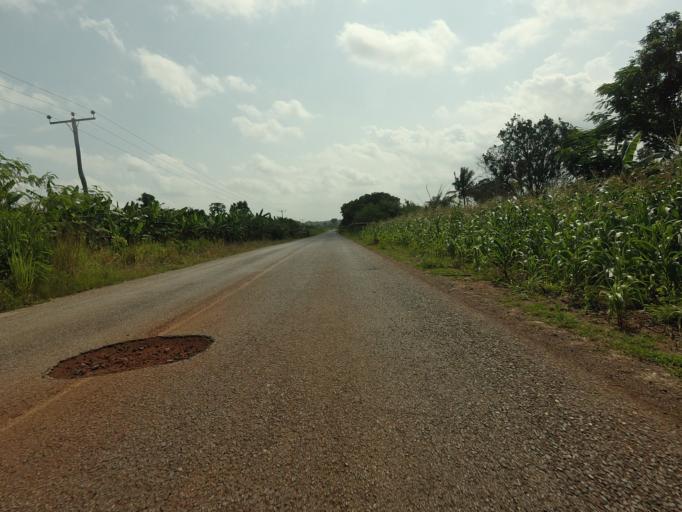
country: TG
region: Maritime
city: Tsevie
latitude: 6.3927
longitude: 0.8163
